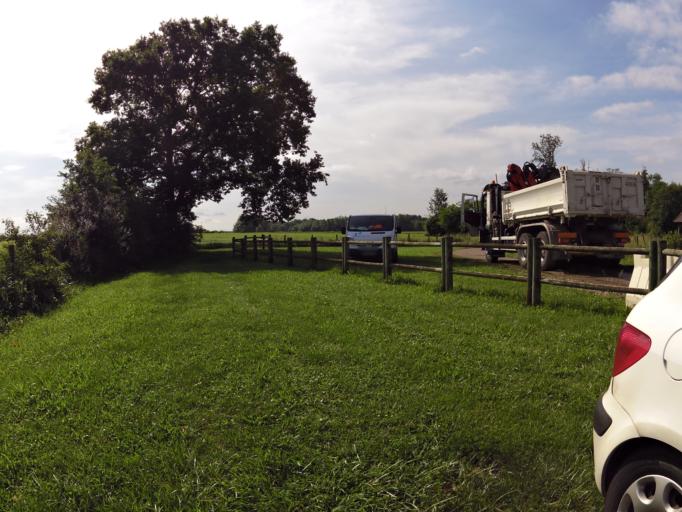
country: FR
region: Champagne-Ardenne
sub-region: Departement de l'Aube
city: Verrieres
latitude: 48.2664
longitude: 4.1795
